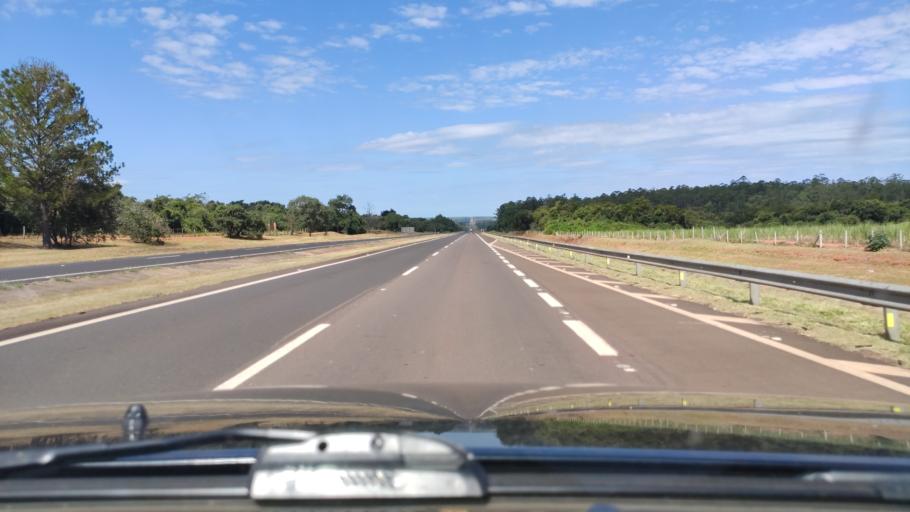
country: BR
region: Sao Paulo
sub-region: Rancharia
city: Rancharia
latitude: -22.4628
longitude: -50.9613
